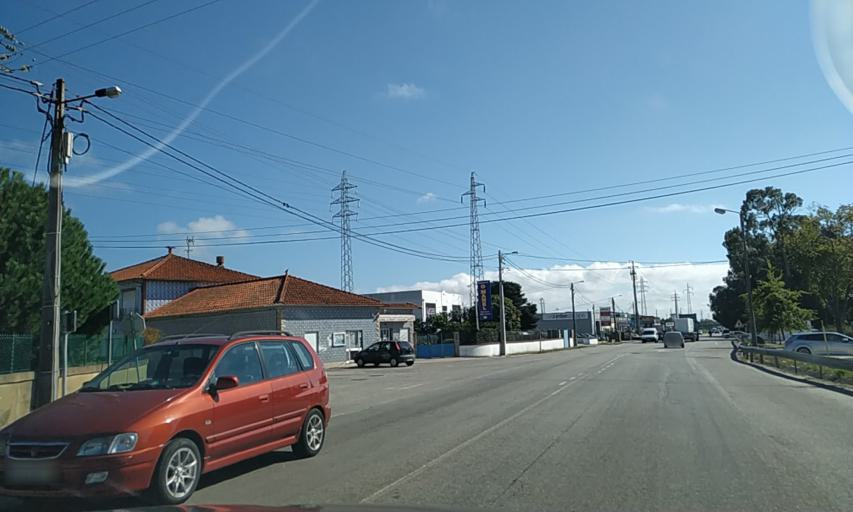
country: PT
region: Aveiro
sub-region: Aveiro
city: Aveiro
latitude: 40.6599
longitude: -8.6143
